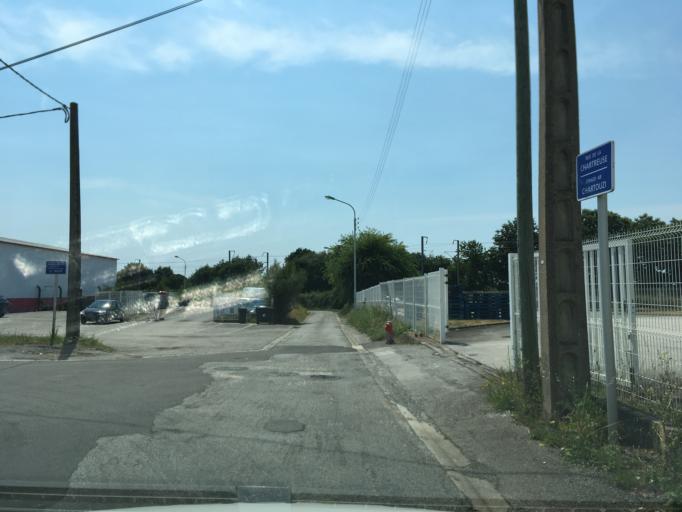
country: FR
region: Brittany
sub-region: Departement du Morbihan
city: Queven
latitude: 47.7674
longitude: -3.4055
